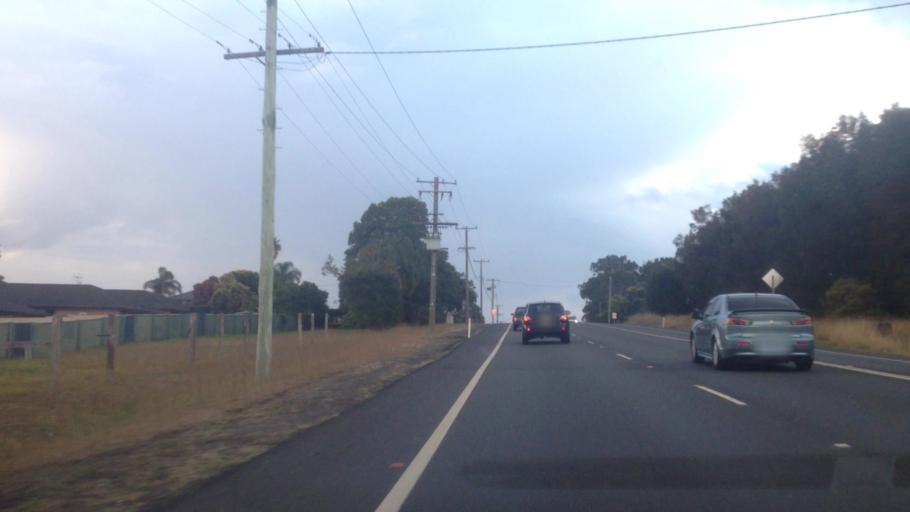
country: AU
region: New South Wales
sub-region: Wyong Shire
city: Kanwal
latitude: -33.2606
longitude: 151.4843
